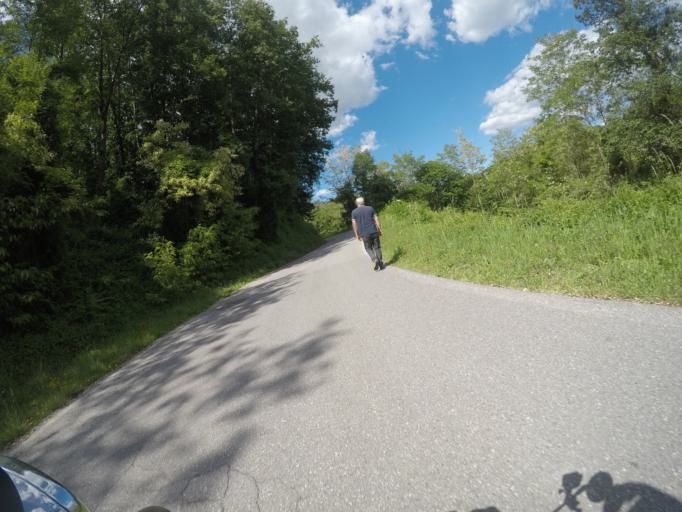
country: IT
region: Tuscany
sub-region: Provincia di Lucca
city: Minucciano
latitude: 44.1652
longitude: 10.2011
